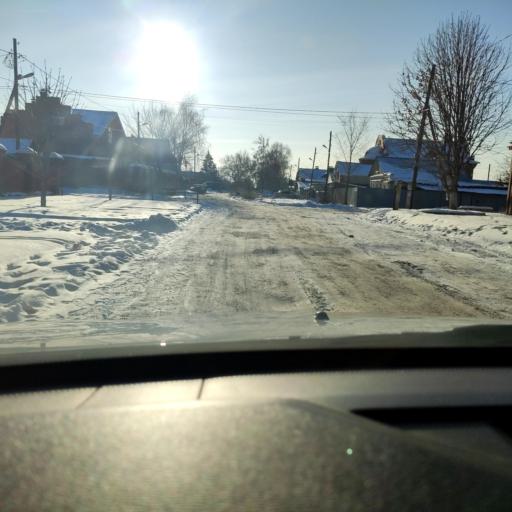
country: RU
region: Samara
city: Petra-Dubrava
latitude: 53.2519
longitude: 50.3223
